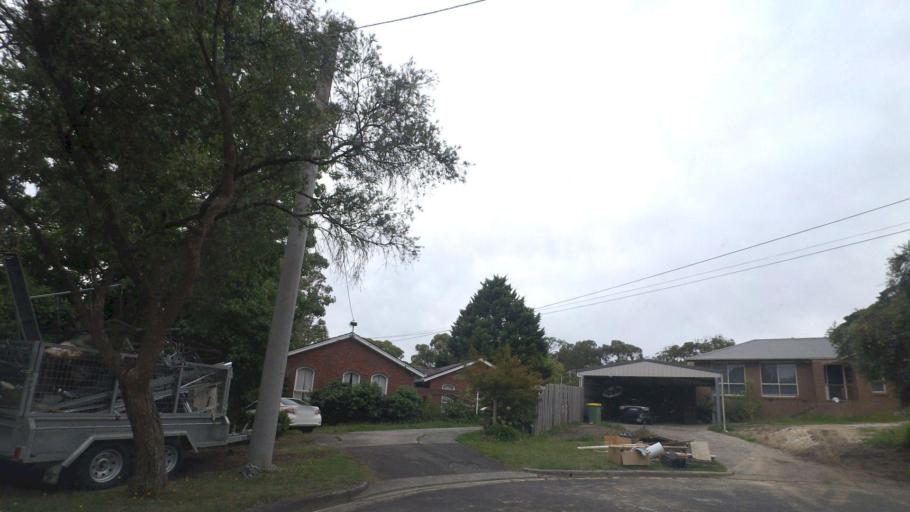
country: AU
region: Victoria
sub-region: Yarra Ranges
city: Kilsyth
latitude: -37.7998
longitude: 145.3265
